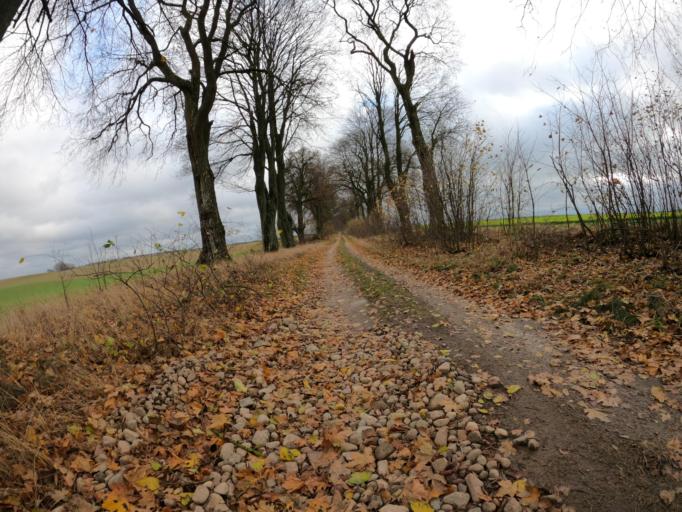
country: PL
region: West Pomeranian Voivodeship
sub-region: Powiat walecki
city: Tuczno
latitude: 53.2560
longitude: 16.1973
